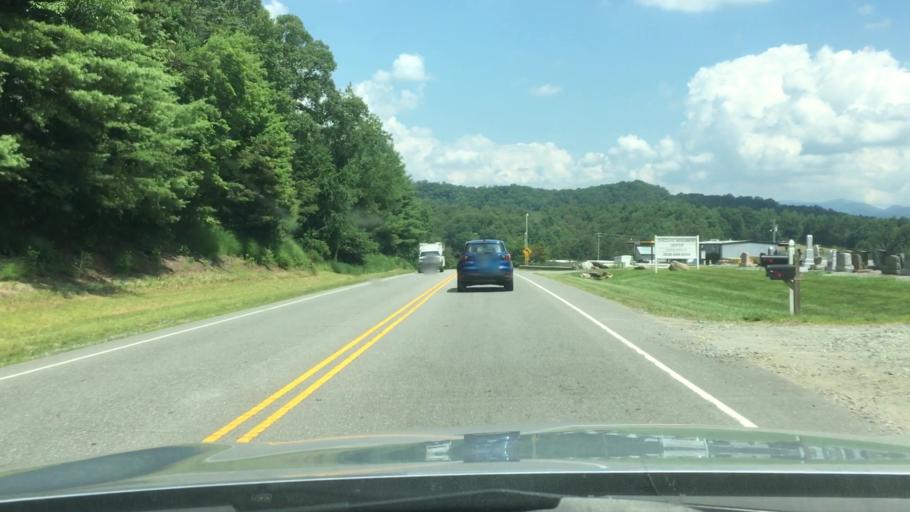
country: US
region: North Carolina
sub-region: Madison County
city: Mars Hill
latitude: 35.8253
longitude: -82.5682
